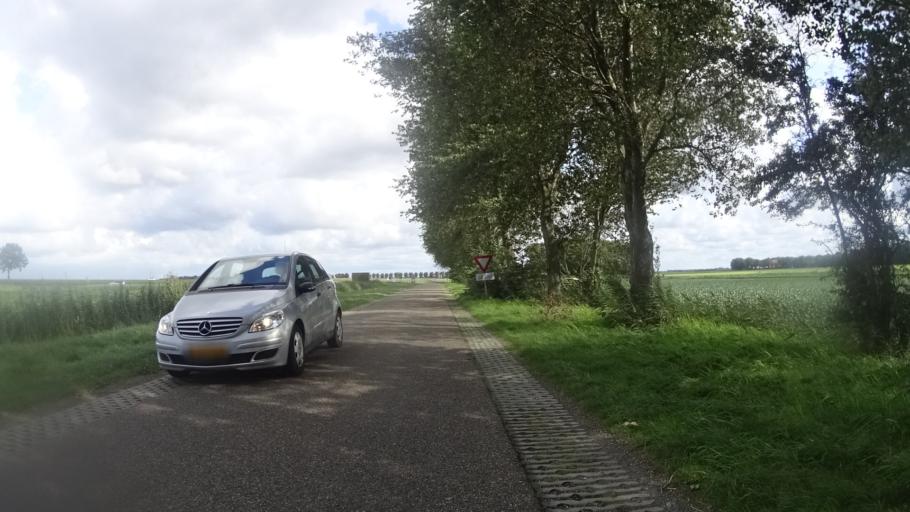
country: NL
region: North Holland
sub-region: Gemeente Hollands Kroon
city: Den Oever
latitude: 52.8828
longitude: 4.9358
